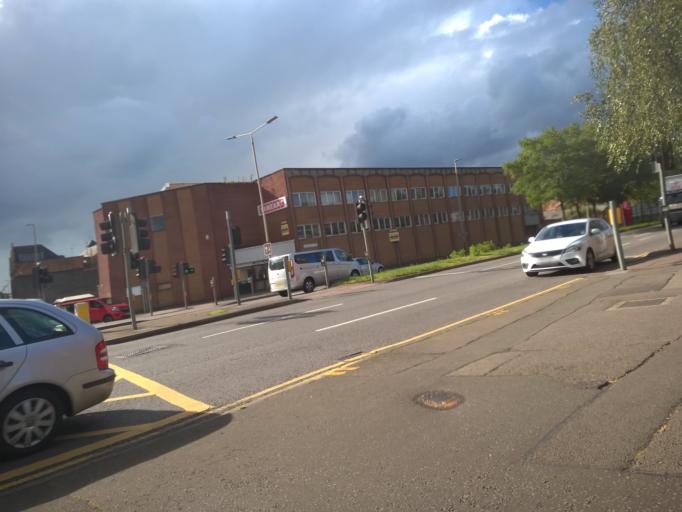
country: GB
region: England
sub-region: City of Leicester
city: Leicester
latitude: 52.6406
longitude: -1.1369
